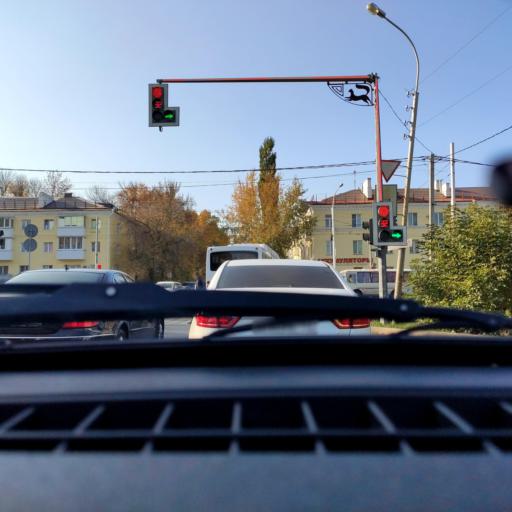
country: RU
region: Bashkortostan
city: Ufa
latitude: 54.8227
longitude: 56.1116
